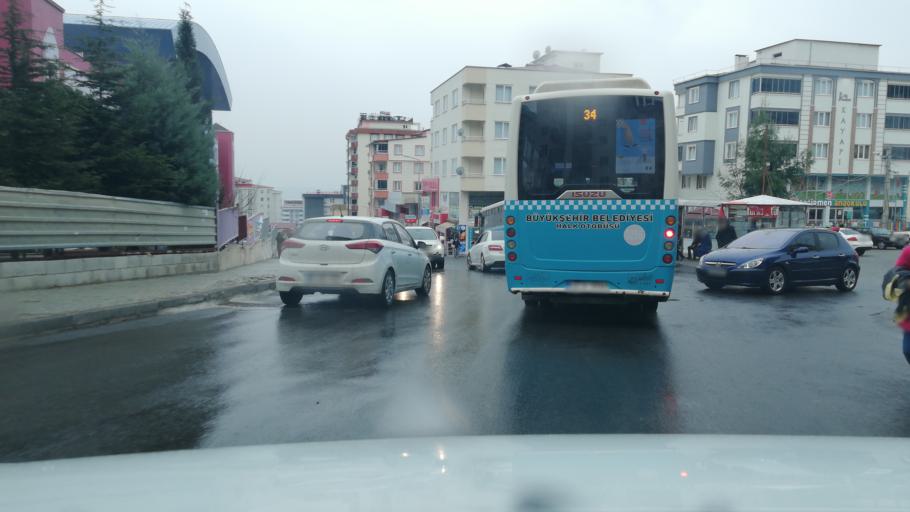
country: TR
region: Kahramanmaras
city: Kahramanmaras
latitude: 37.5948
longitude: 36.8832
